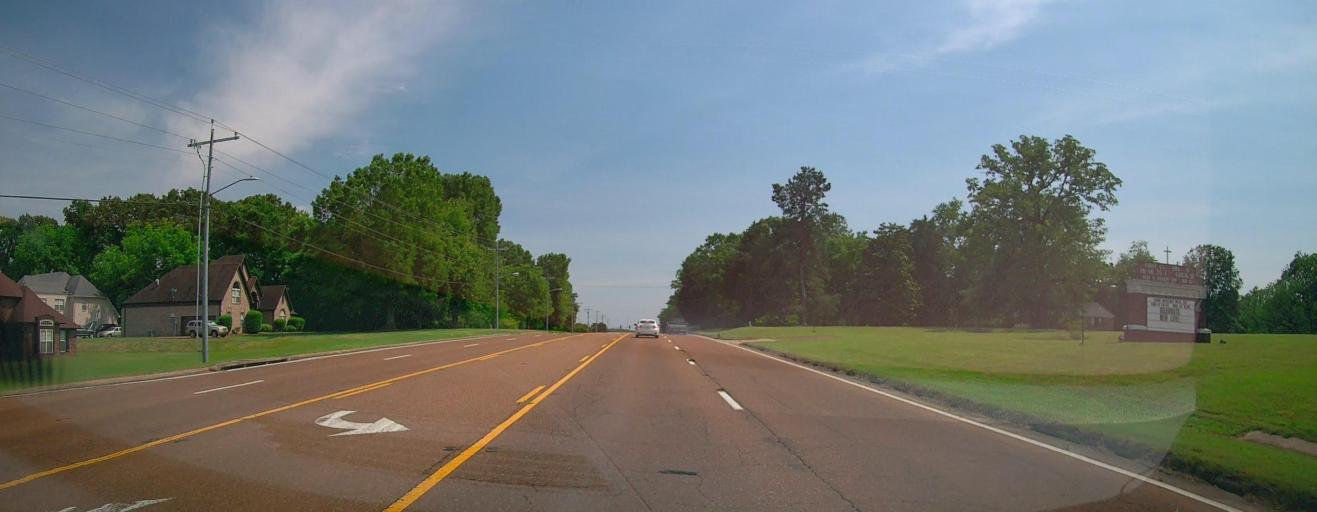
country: US
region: Mississippi
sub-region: De Soto County
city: Olive Branch
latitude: 34.9799
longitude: -89.8306
